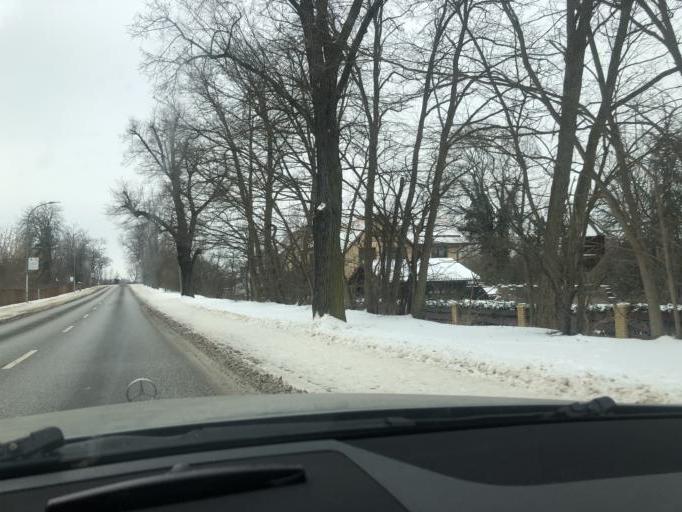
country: DE
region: Brandenburg
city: Guben
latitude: 51.9567
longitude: 14.7063
